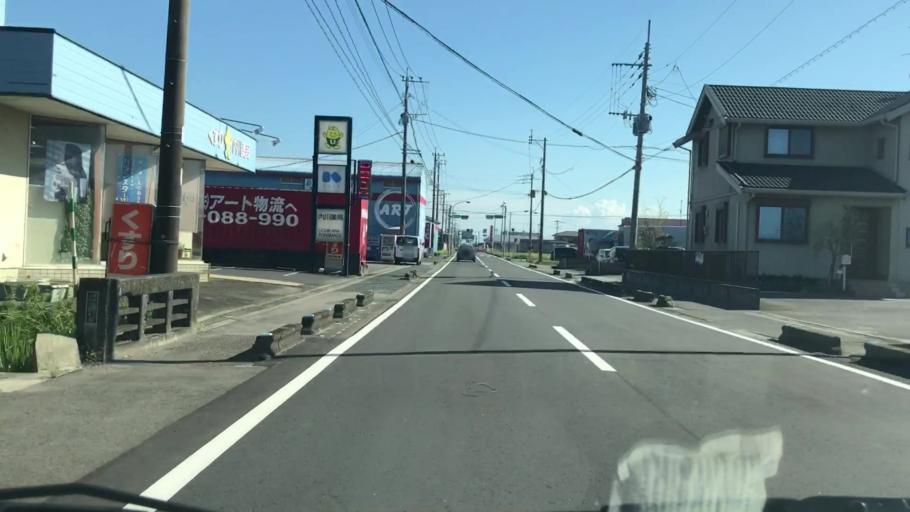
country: JP
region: Saga Prefecture
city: Okawa
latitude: 33.2094
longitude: 130.3354
